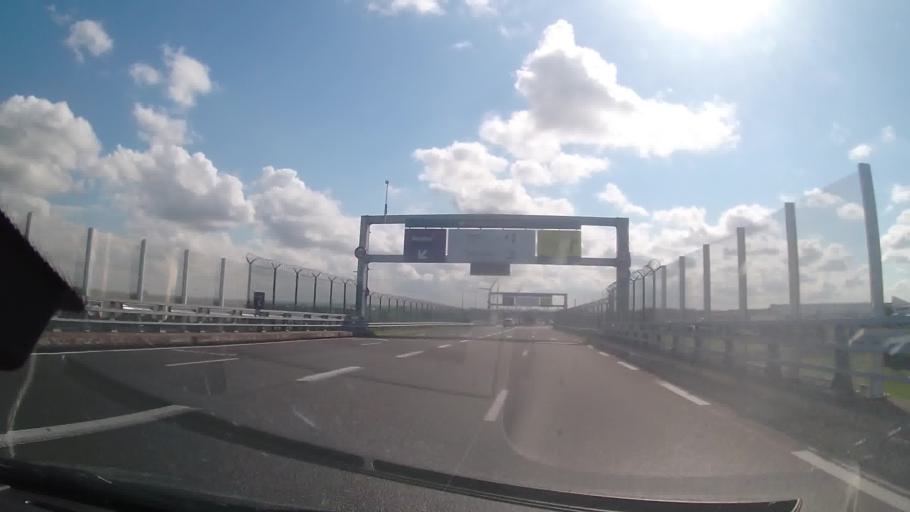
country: FR
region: Nord-Pas-de-Calais
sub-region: Departement du Pas-de-Calais
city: Coquelles
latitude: 50.9397
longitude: 1.8156
